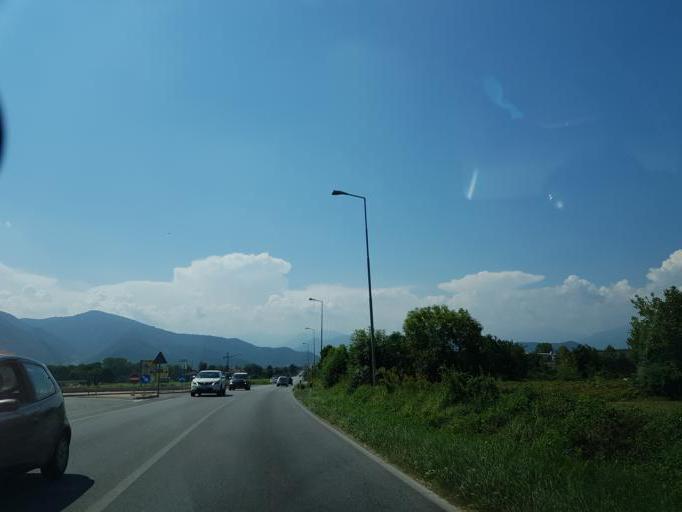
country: IT
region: Piedmont
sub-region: Provincia di Cuneo
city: San Rocco
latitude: 44.3981
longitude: 7.4702
